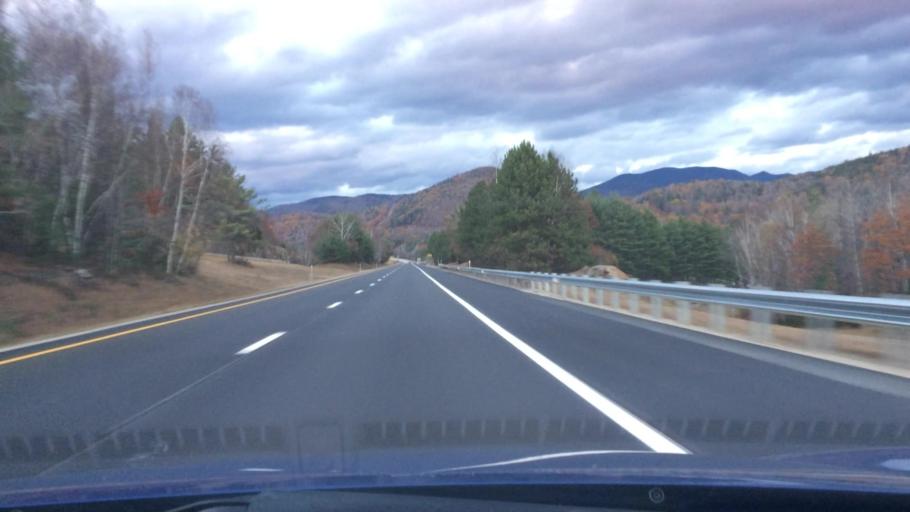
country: US
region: New Hampshire
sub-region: Grafton County
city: Woodstock
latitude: 43.9525
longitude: -71.6835
